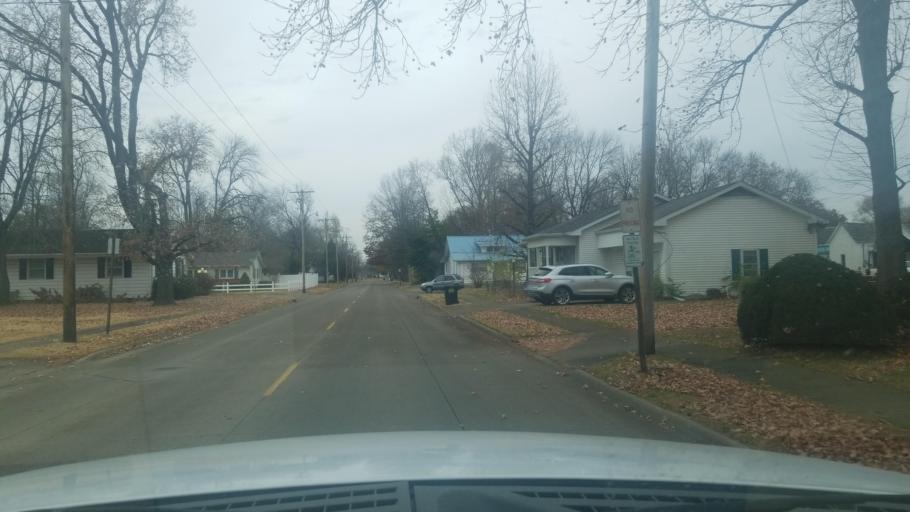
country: US
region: Illinois
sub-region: Saline County
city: Harrisburg
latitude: 37.7317
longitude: -88.5529
